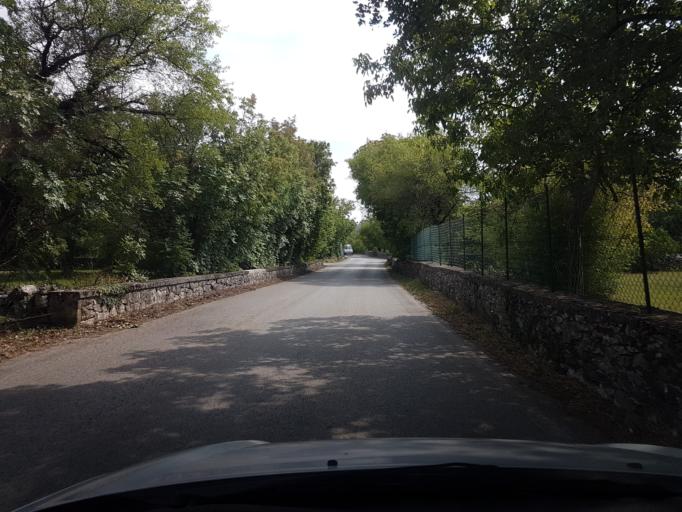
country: IT
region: Friuli Venezia Giulia
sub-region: Provincia di Trieste
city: Villa Opicina
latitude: 45.7093
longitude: 13.7709
